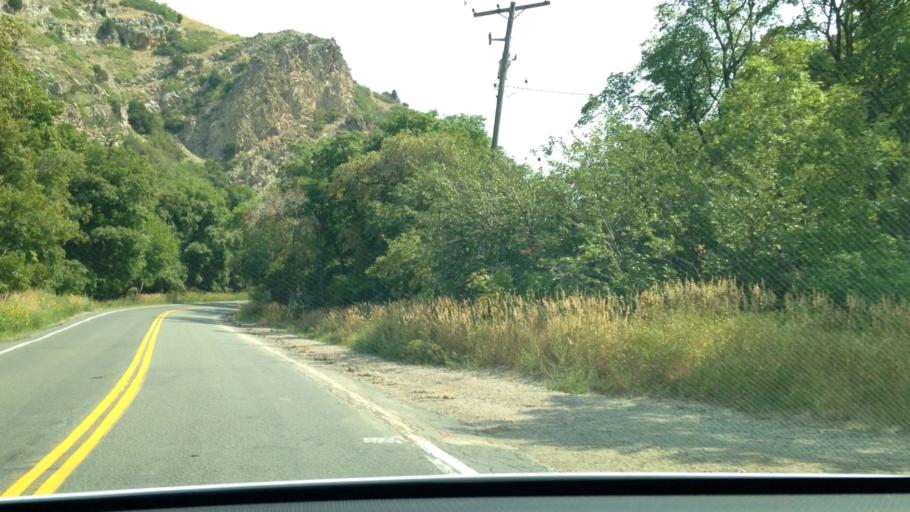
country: US
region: Utah
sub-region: Salt Lake County
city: Mount Olympus
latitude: 40.6907
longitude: -111.7640
